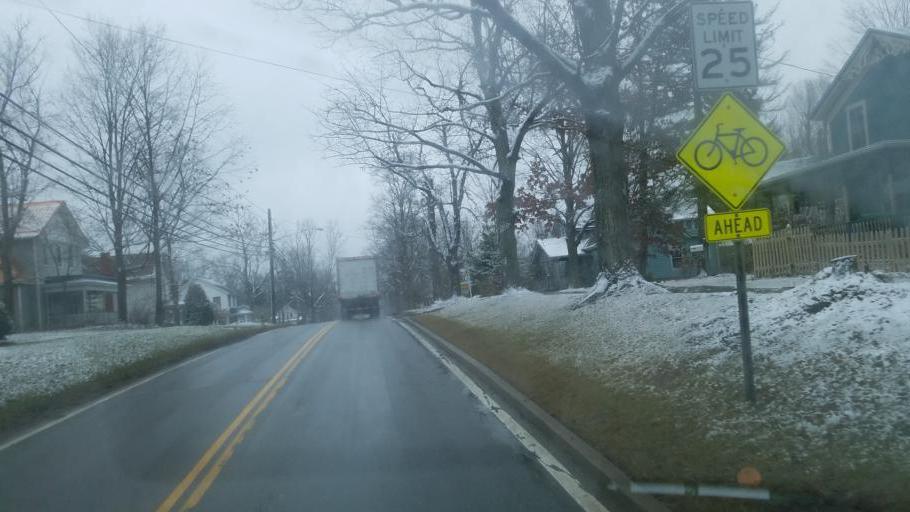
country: US
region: Ohio
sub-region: Portage County
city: Garrettsville
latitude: 41.2803
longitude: -81.0985
